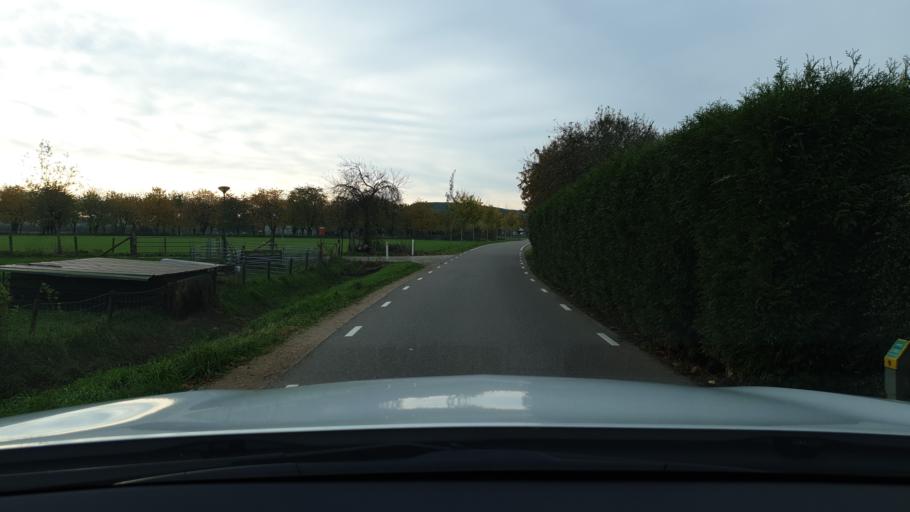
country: NL
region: Gelderland
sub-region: Gemeente Nijmegen
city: Lindenholt
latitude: 51.8589
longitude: 5.7982
